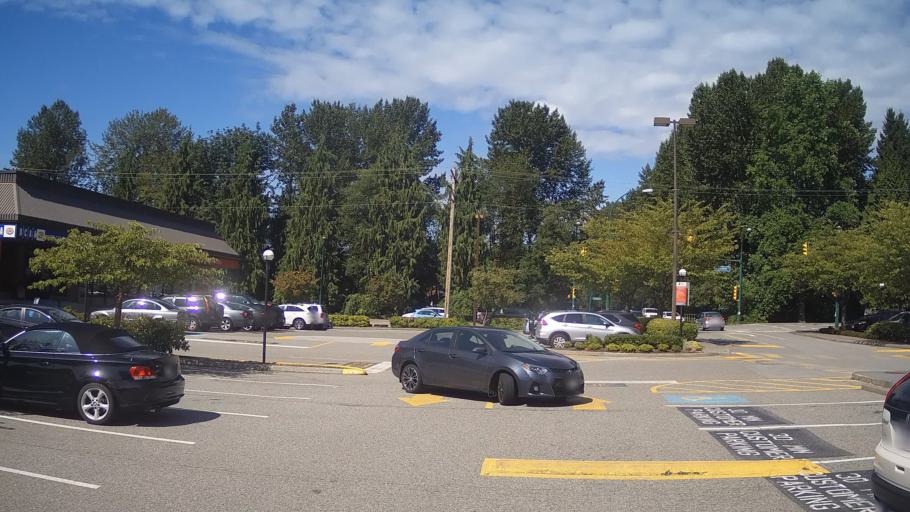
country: CA
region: British Columbia
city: Port Moody
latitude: 49.2787
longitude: -122.8073
